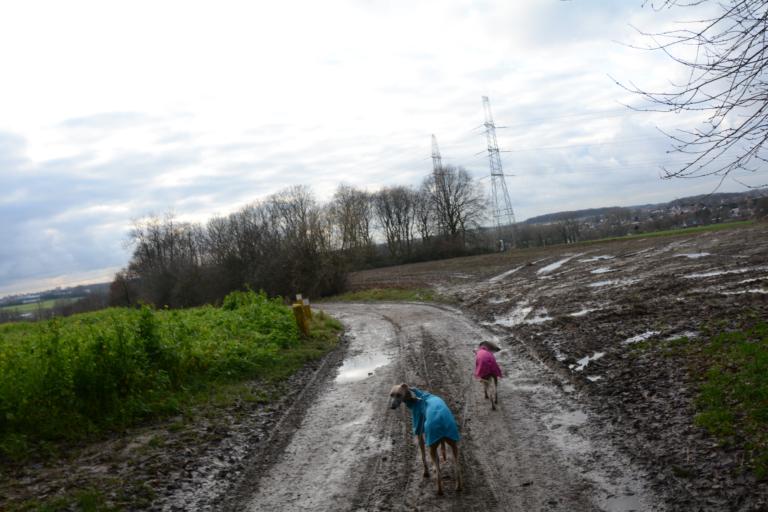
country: BE
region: Flanders
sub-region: Provincie Vlaams-Brabant
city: Merchtem
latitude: 50.9326
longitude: 4.2381
